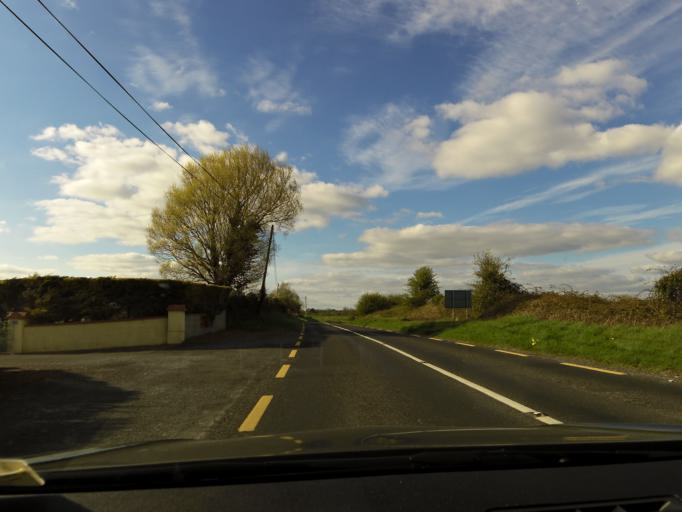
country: IE
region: Connaught
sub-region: County Galway
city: Portumna
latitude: 53.1096
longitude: -8.2362
